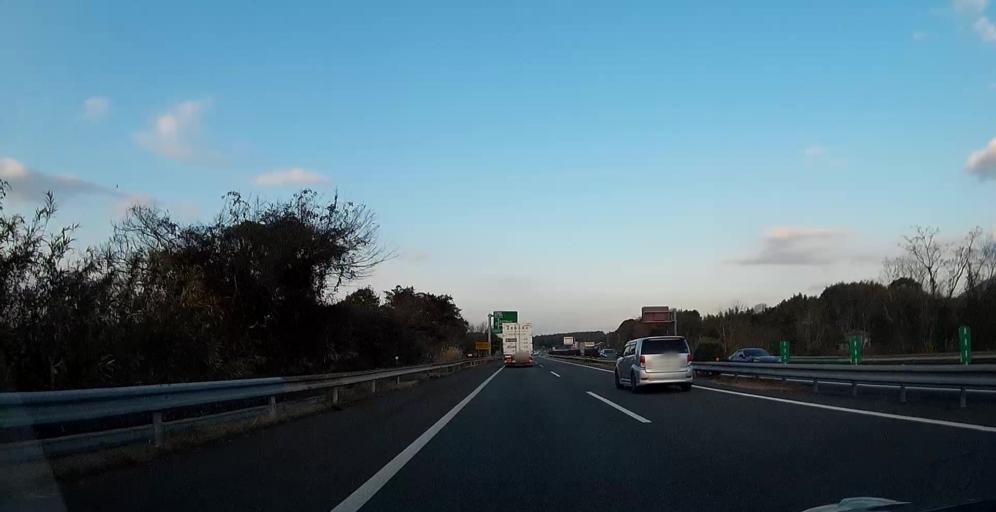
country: JP
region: Kumamoto
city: Kumamoto
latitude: 32.7378
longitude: 130.7799
